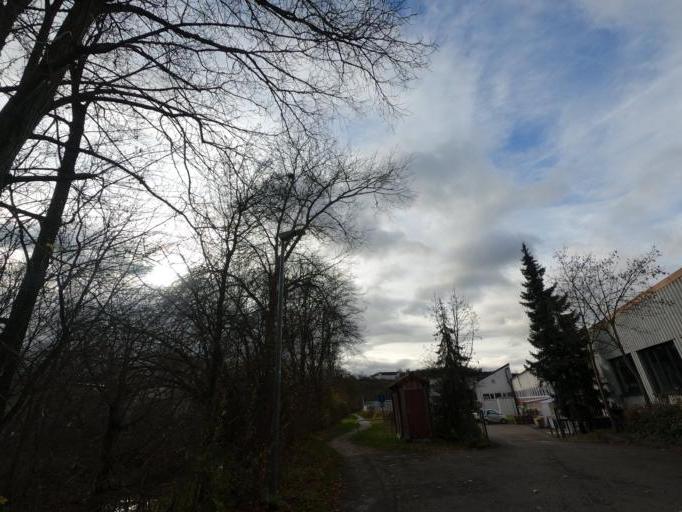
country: DE
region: Baden-Wuerttemberg
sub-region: Regierungsbezirk Stuttgart
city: Wangen
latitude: 48.7068
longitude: 9.6105
